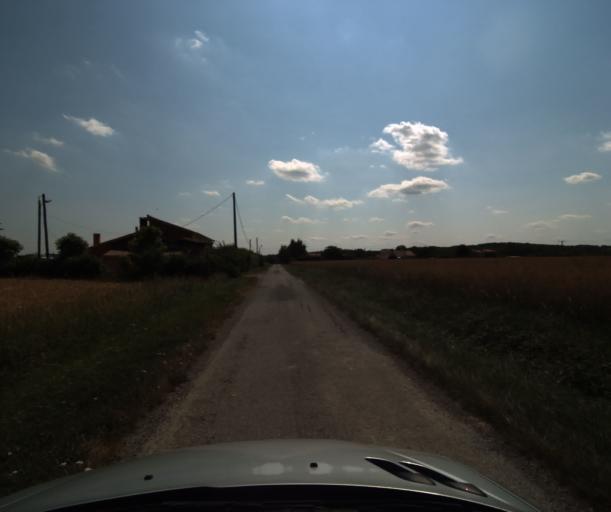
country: FR
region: Midi-Pyrenees
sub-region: Departement de la Haute-Garonne
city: Saint-Lys
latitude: 43.5282
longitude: 1.1661
